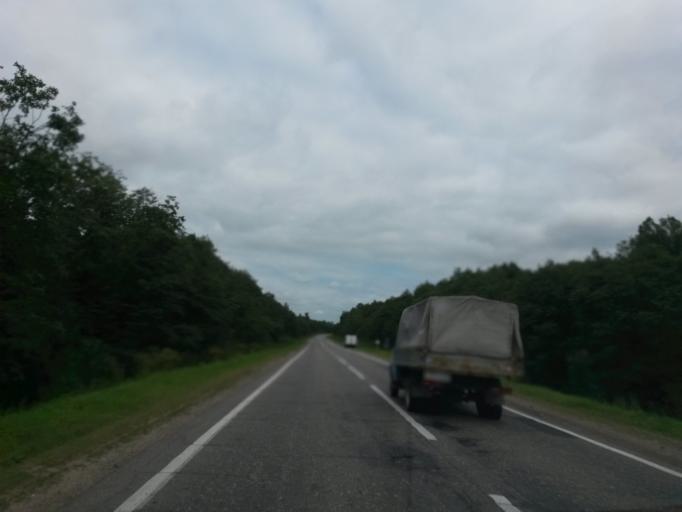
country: RU
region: Jaroslavl
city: Krasnyye Tkachi
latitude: 57.4854
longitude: 39.9031
